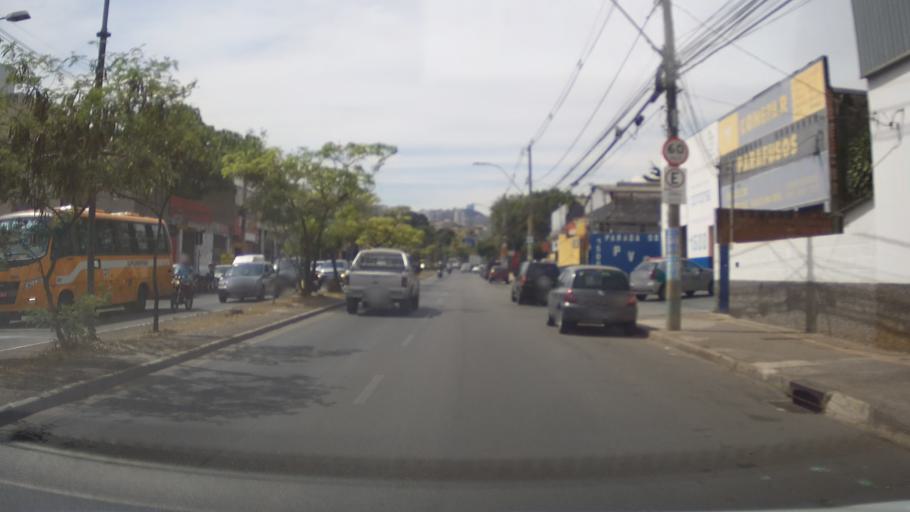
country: BR
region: Minas Gerais
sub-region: Belo Horizonte
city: Belo Horizonte
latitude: -19.9495
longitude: -43.9690
